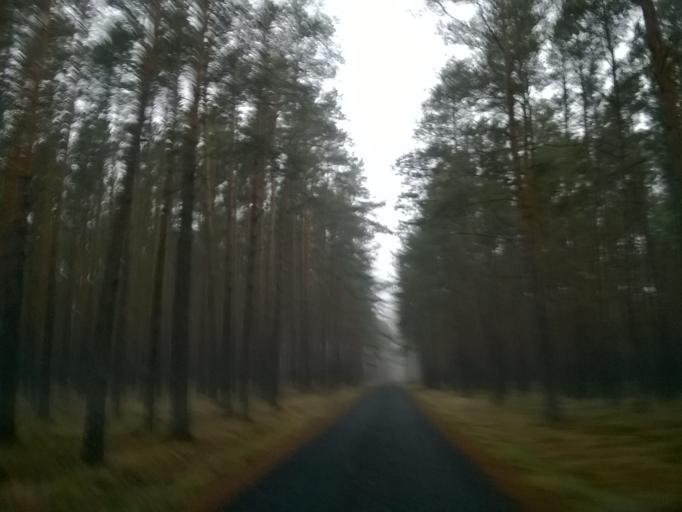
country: PL
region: Kujawsko-Pomorskie
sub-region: Powiat nakielski
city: Kcynia
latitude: 53.0540
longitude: 17.4272
